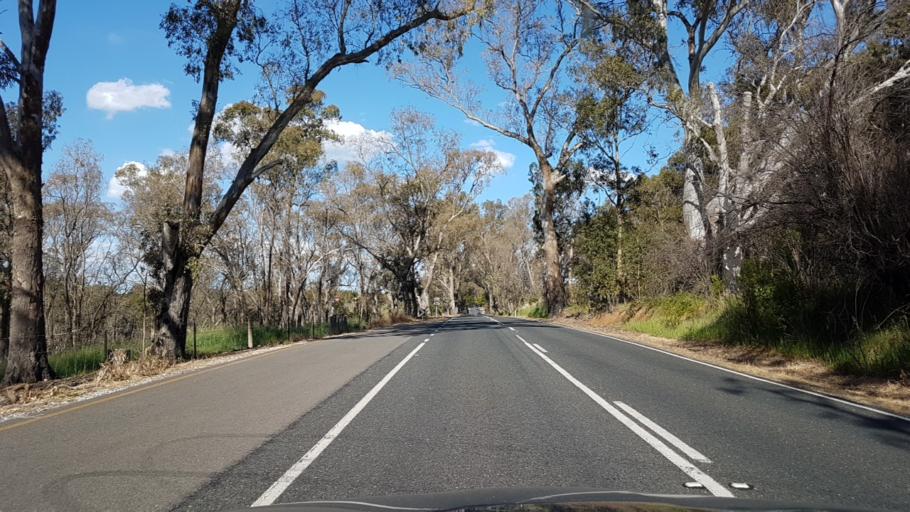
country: AU
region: South Australia
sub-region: Adelaide Hills
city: Gumeracha
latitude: -34.8201
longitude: 138.8610
